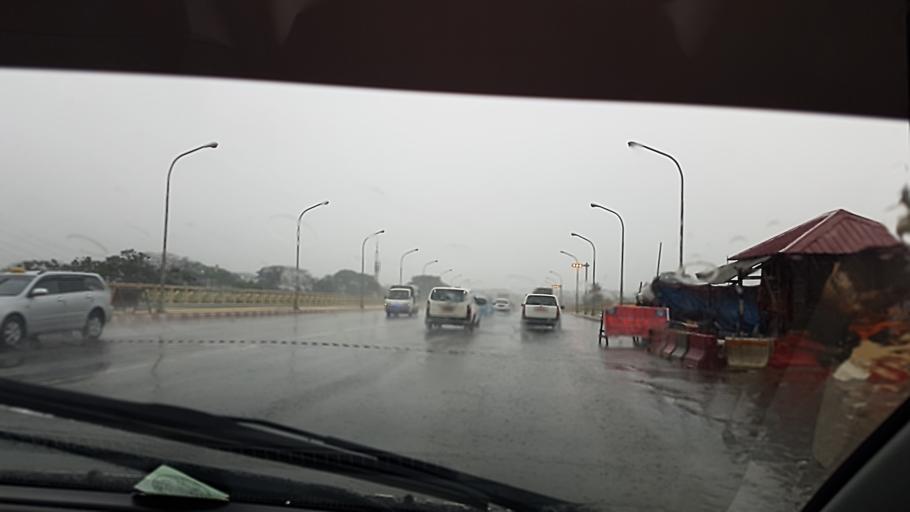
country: MM
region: Yangon
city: Yangon
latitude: 16.7778
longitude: 96.1837
